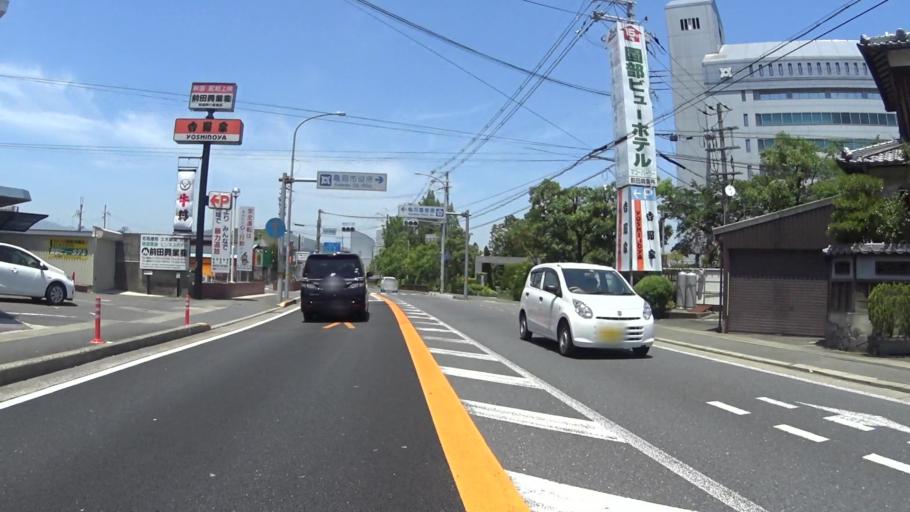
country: JP
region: Kyoto
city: Kameoka
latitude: 35.0126
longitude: 135.5734
